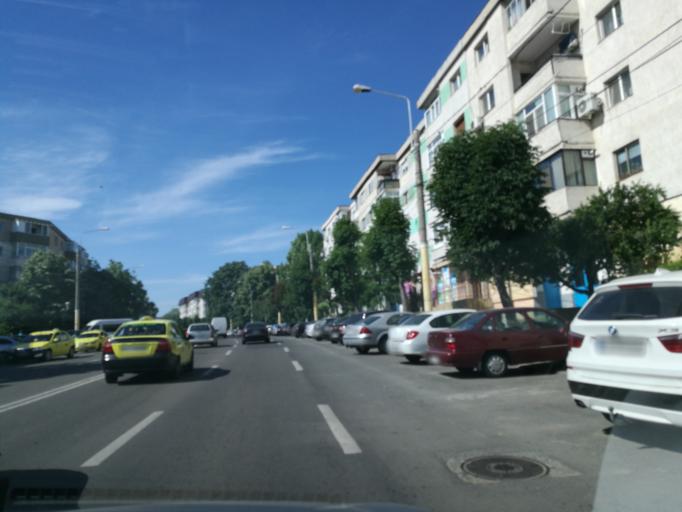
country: RO
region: Constanta
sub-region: Municipiul Constanta
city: Constanta
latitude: 44.1990
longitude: 28.6250
